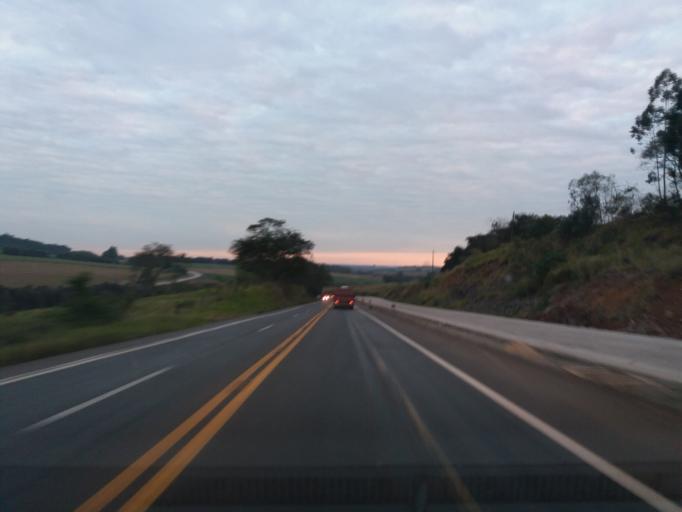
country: BR
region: Parana
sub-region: Realeza
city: Realeza
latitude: -25.3792
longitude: -53.5760
